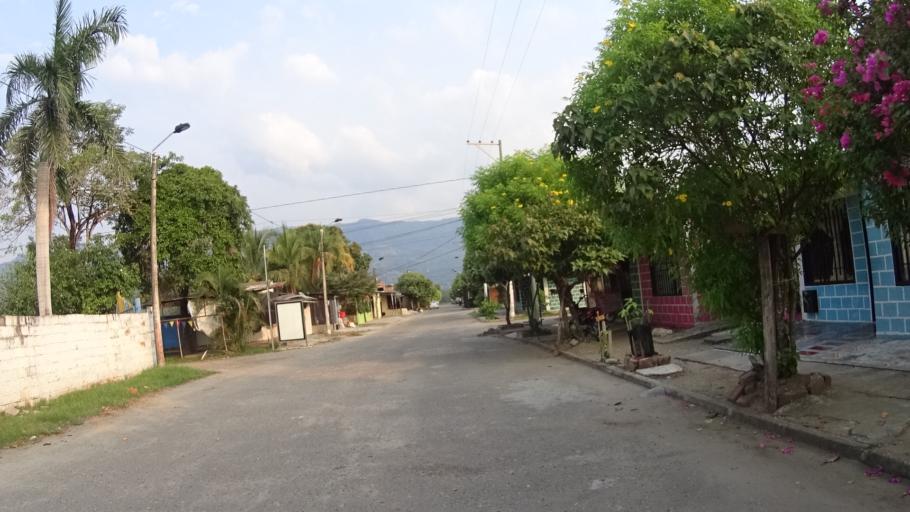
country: CO
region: Caldas
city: La Dorada
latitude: 5.4431
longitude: -74.6565
